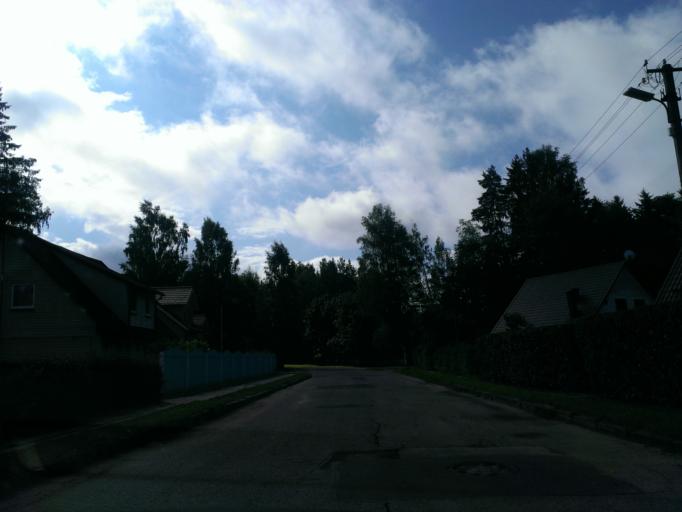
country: LV
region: Incukalns
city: Vangazi
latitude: 57.0943
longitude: 24.5513
